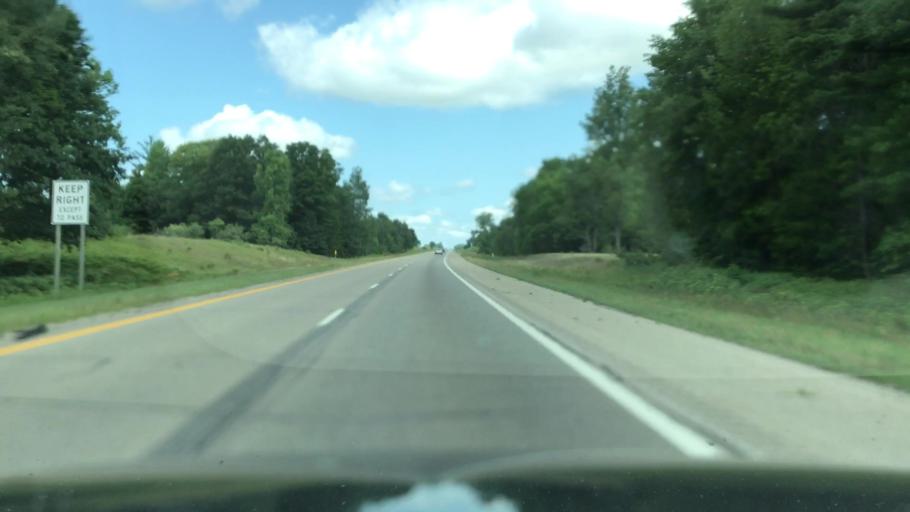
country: US
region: Michigan
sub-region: Mecosta County
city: Big Rapids
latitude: 43.7023
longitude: -85.5277
